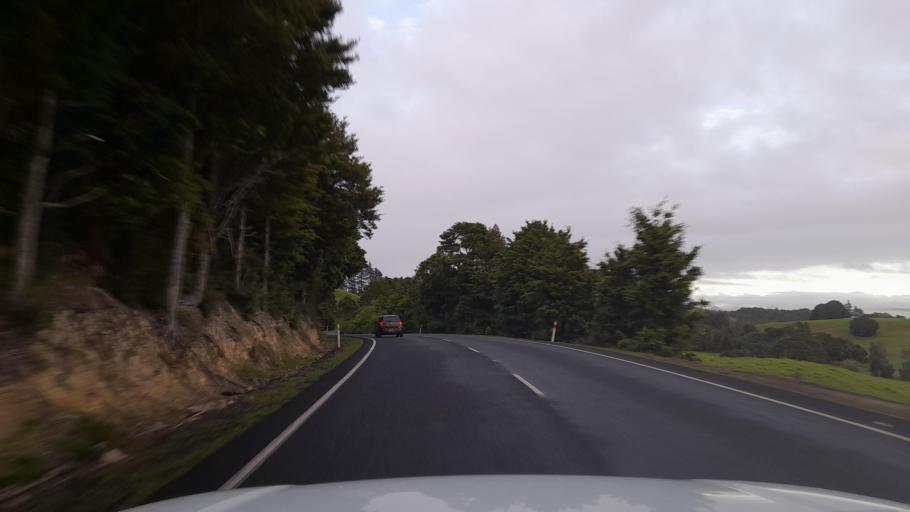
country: NZ
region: Northland
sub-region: Whangarei
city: Maungatapere
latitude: -35.7068
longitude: 174.0094
